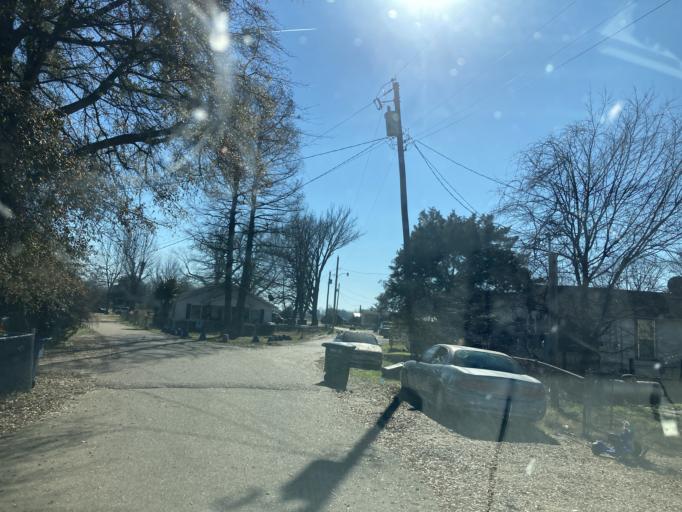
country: US
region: Mississippi
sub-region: Yazoo County
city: Yazoo City
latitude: 32.9763
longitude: -90.5923
